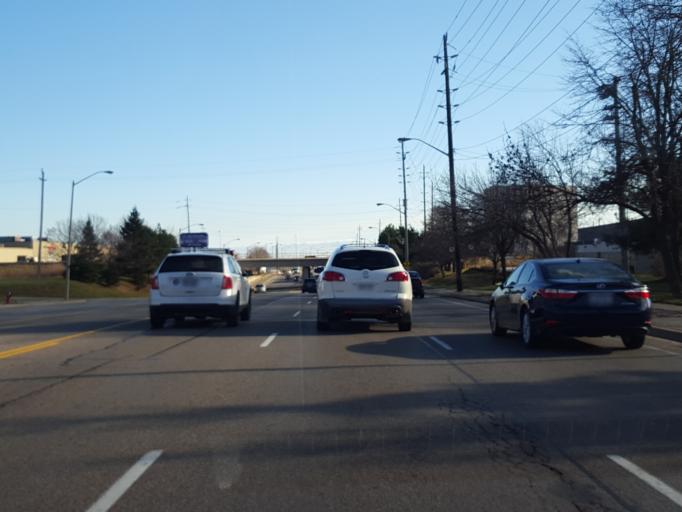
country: CA
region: Ontario
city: Burlington
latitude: 43.3707
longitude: -79.7942
